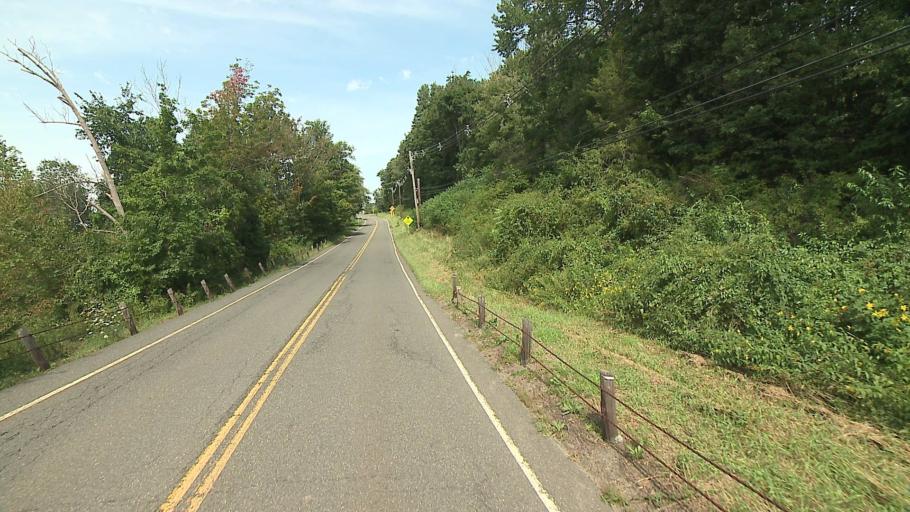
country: US
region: Connecticut
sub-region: Litchfield County
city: Bethlehem Village
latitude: 41.6172
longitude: -73.2455
